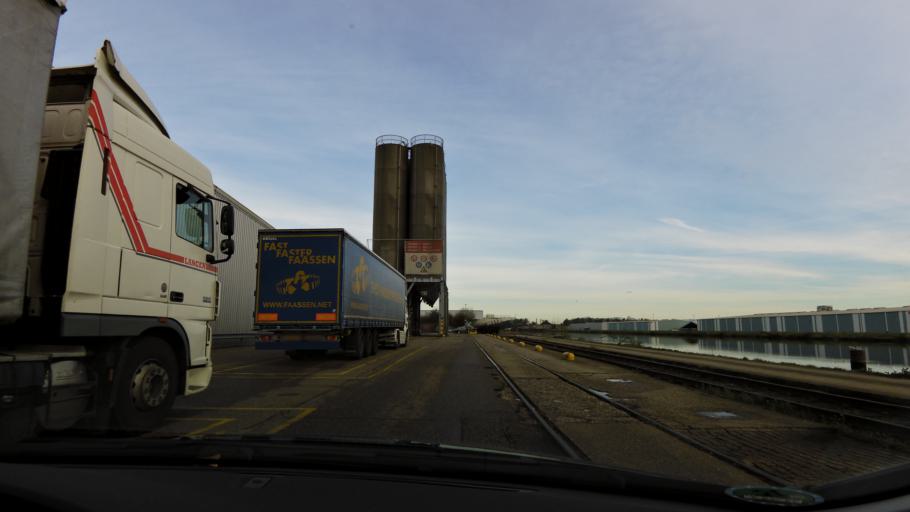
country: NL
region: Limburg
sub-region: Gemeente Sittard-Geleen
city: Born
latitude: 51.0500
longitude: 5.8103
